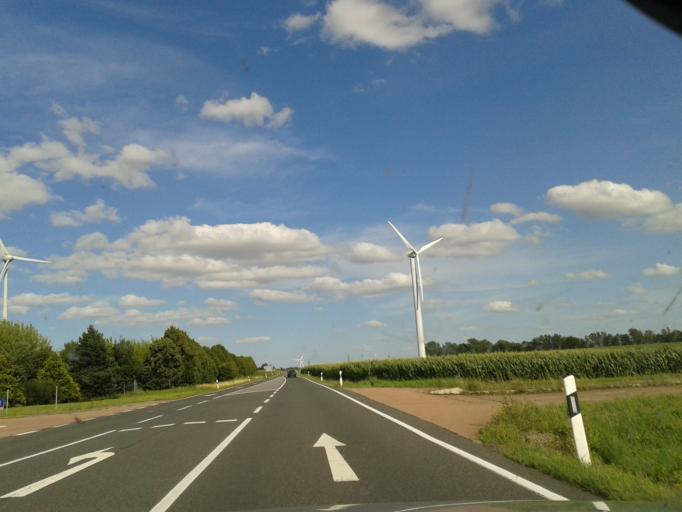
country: DE
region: Saxony-Anhalt
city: Polleben
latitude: 51.5767
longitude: 11.6160
